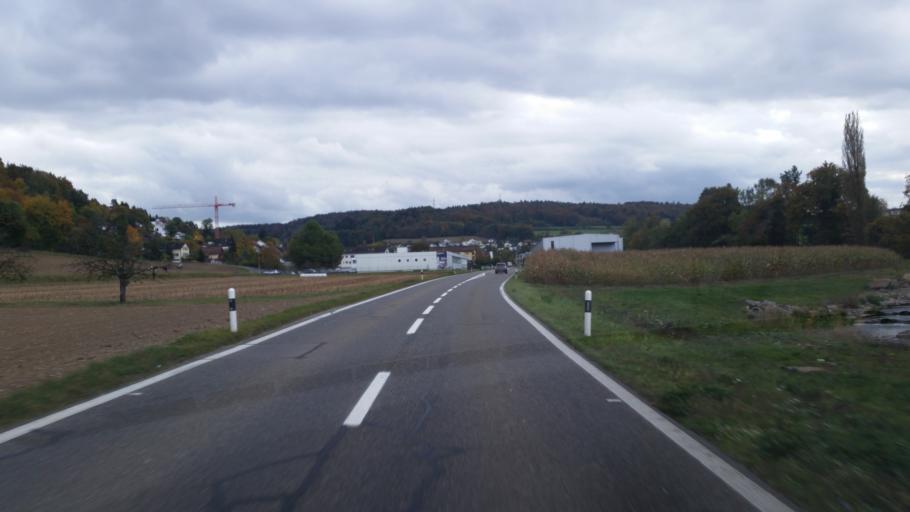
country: CH
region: Aargau
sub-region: Bezirk Zurzach
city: Oberendingen
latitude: 47.5448
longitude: 8.2900
